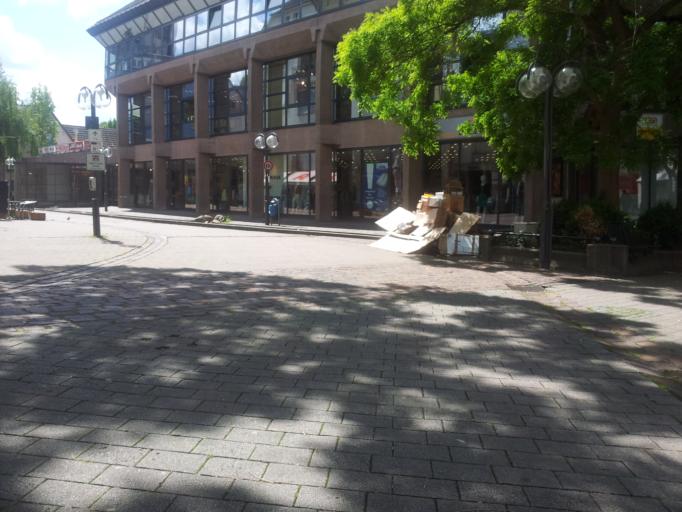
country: DE
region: Baden-Wuerttemberg
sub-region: Regierungsbezirk Stuttgart
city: Plochingen
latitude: 48.7109
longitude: 9.4159
